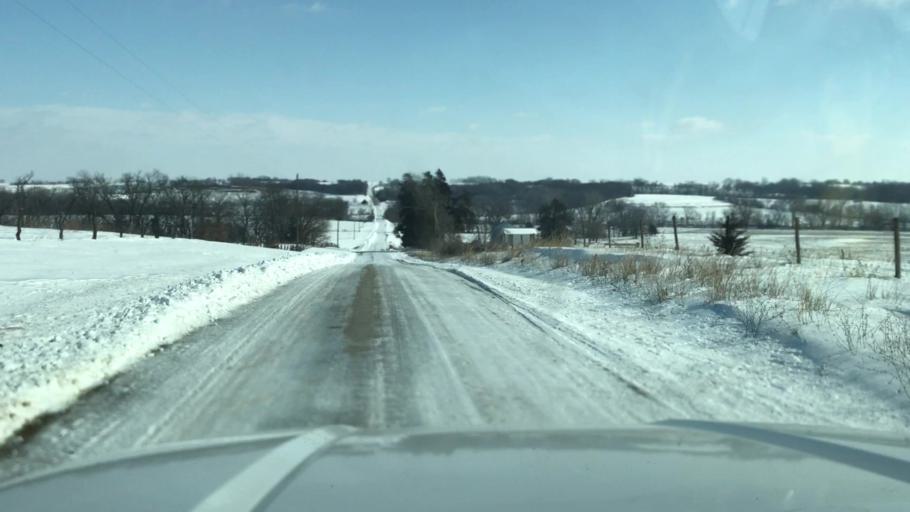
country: US
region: Missouri
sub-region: Nodaway County
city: Maryville
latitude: 40.3865
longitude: -94.6775
